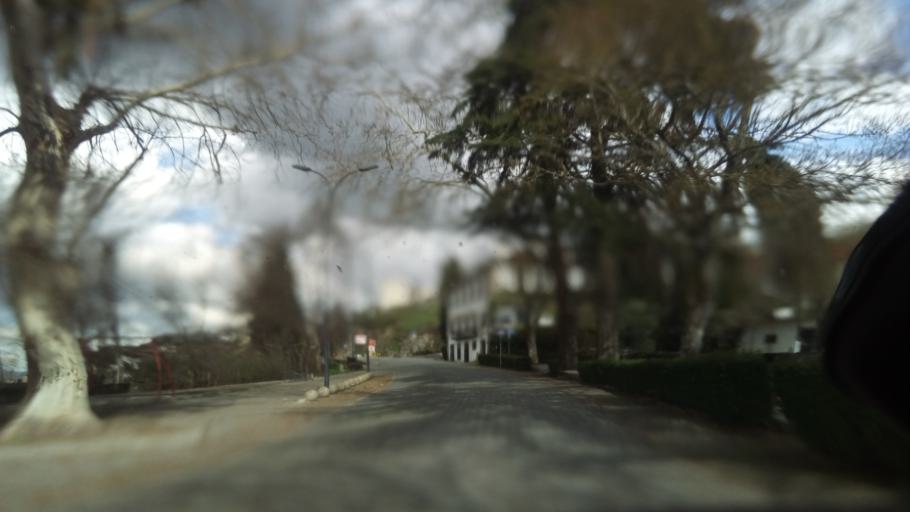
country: PT
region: Guarda
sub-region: Celorico da Beira
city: Celorico da Beira
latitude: 40.6322
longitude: -7.3980
